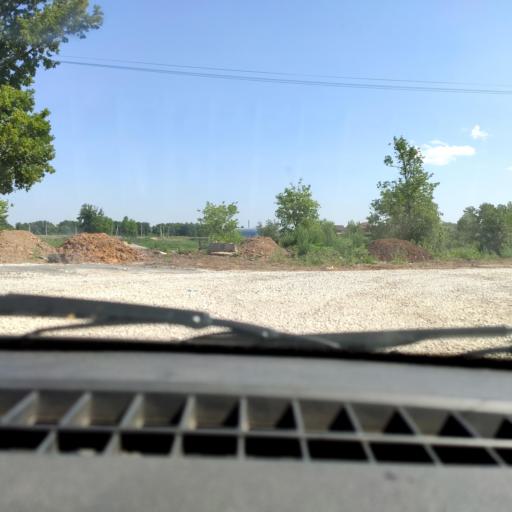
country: RU
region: Bashkortostan
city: Mikhaylovka
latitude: 54.8134
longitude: 55.9353
